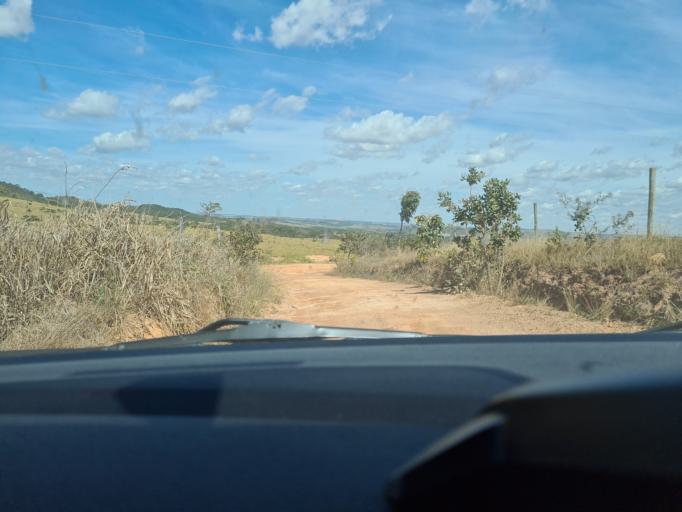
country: BR
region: Goias
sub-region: Silvania
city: Silvania
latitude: -16.5378
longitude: -48.5546
